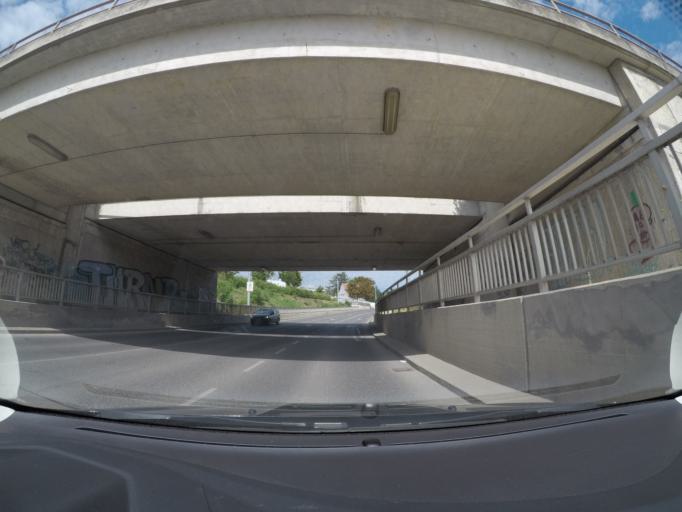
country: AT
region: Lower Austria
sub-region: Politischer Bezirk Modling
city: Perchtoldsdorf
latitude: 48.1517
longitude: 16.2922
